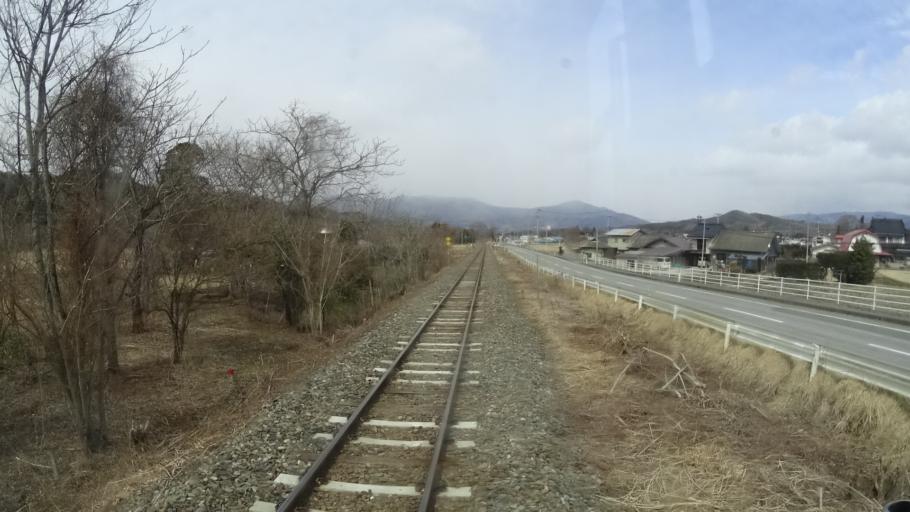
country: JP
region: Iwate
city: Tono
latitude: 39.3160
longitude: 141.5650
